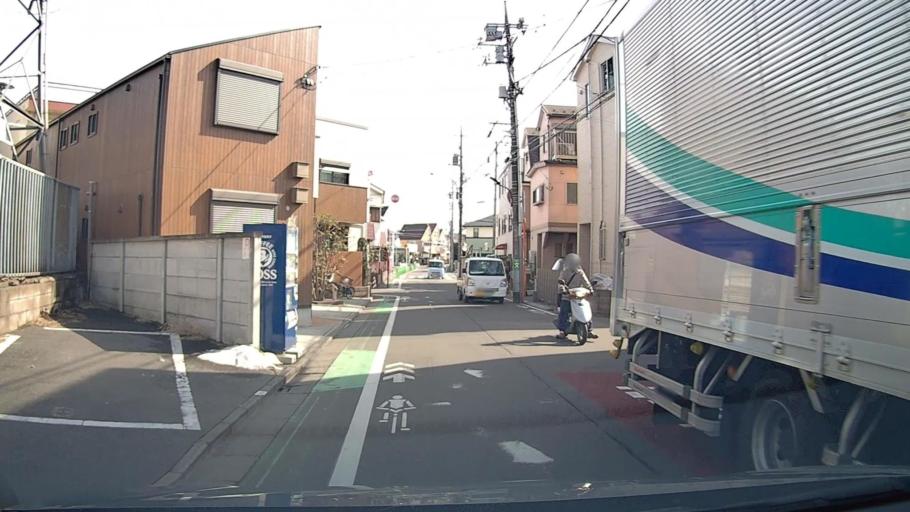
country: JP
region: Tokyo
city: Nishi-Tokyo-shi
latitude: 35.7437
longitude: 139.5731
